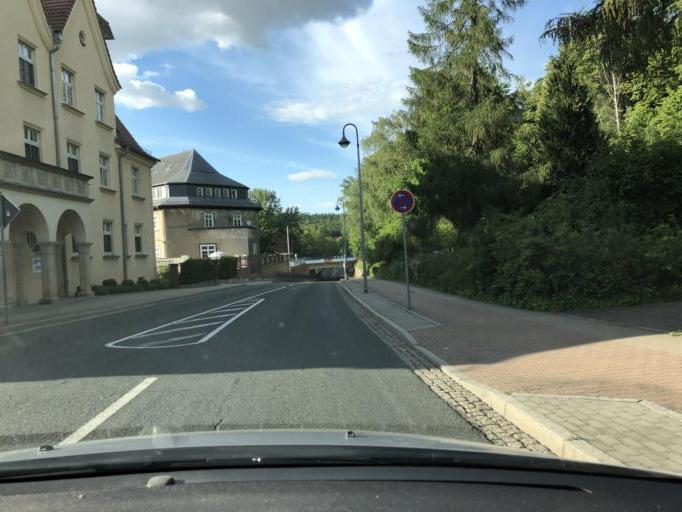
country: DE
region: Thuringia
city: Schmolln
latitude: 50.8995
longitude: 12.3588
